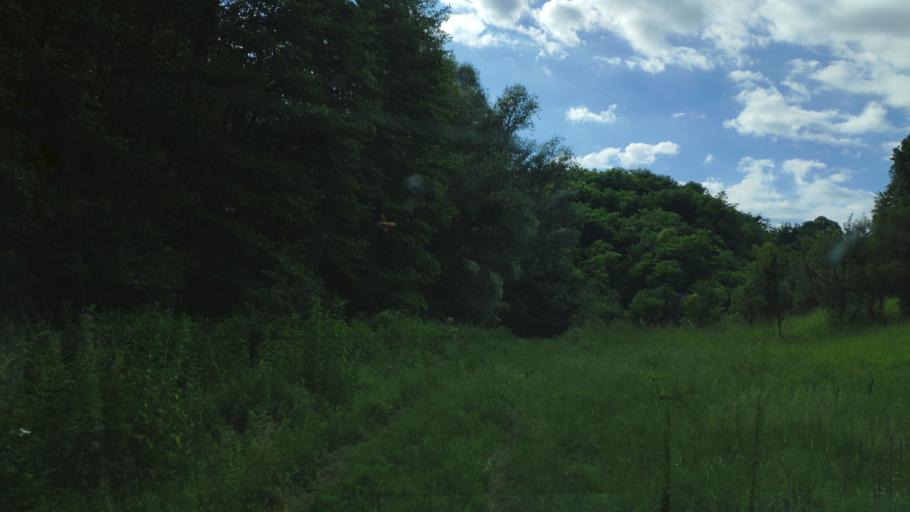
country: HU
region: Borsod-Abauj-Zemplen
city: Arlo
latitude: 48.2556
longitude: 20.1267
